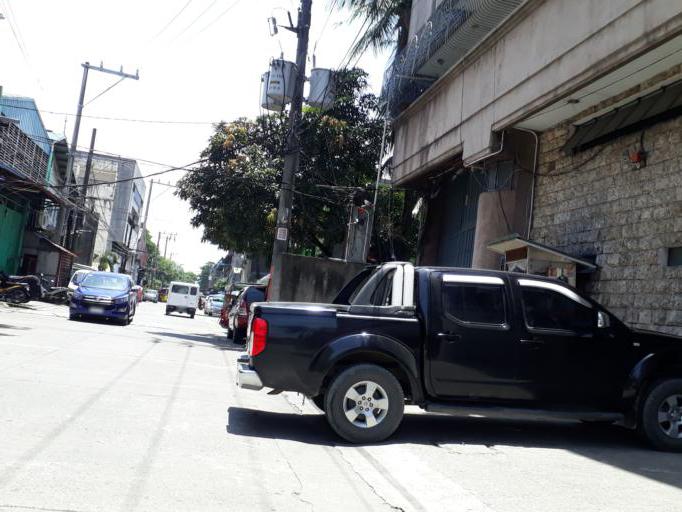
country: PH
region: Metro Manila
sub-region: Caloocan City
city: Niugan
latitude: 14.6500
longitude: 120.9852
